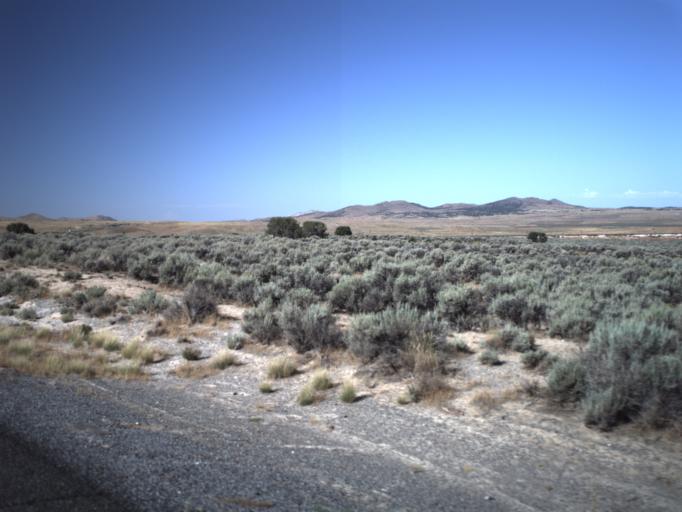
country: US
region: Utah
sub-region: Juab County
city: Mona
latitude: 39.7242
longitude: -112.1972
